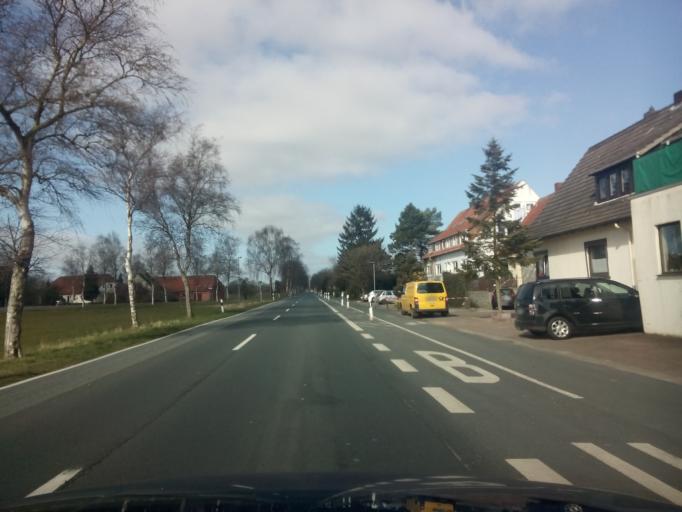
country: DE
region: Lower Saxony
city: Grasberg
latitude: 53.1957
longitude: 8.9772
